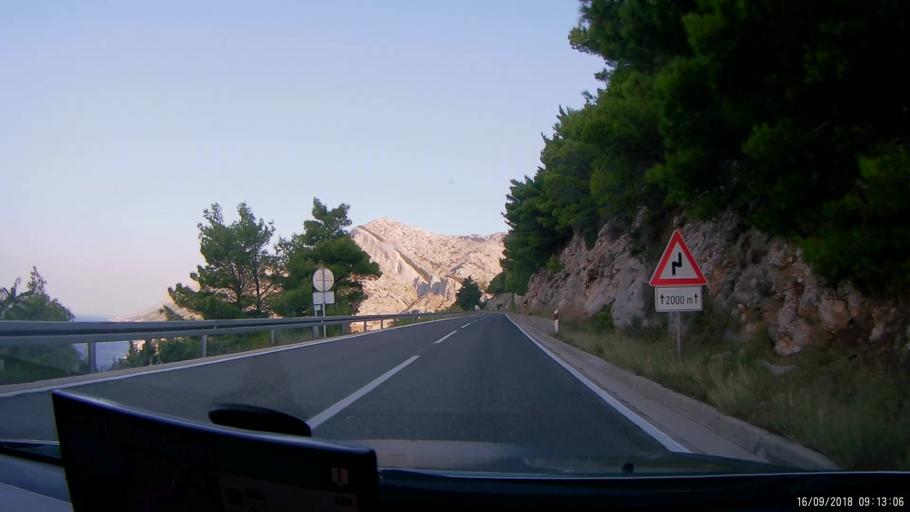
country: HR
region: Splitsko-Dalmatinska
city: Donja Brela
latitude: 43.3943
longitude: 16.8975
